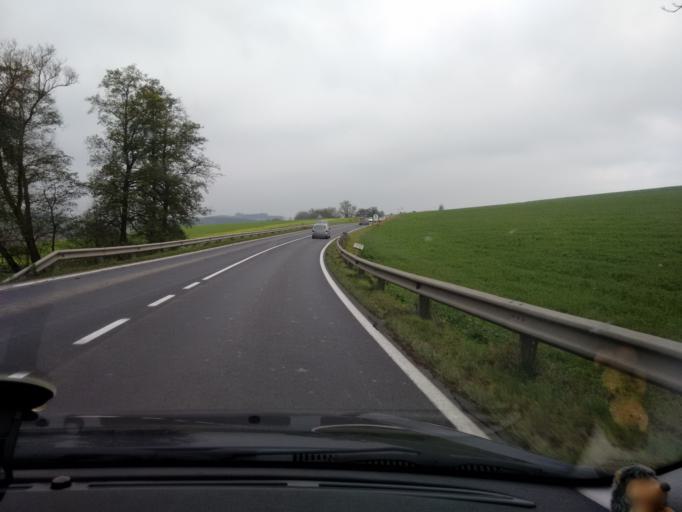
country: AT
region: Upper Austria
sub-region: Wels-Land
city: Buchkirchen
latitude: 48.1975
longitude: 13.9911
